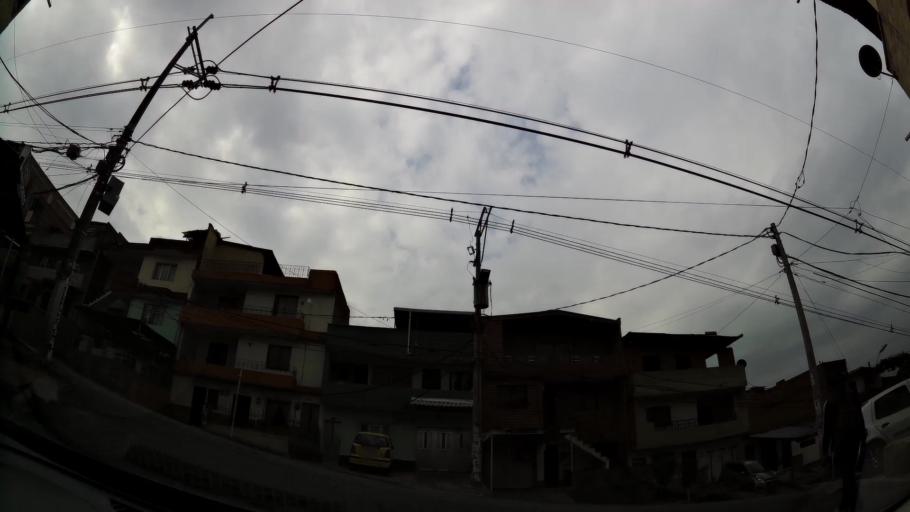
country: CO
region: Antioquia
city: Medellin
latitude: 6.2918
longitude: -75.5587
